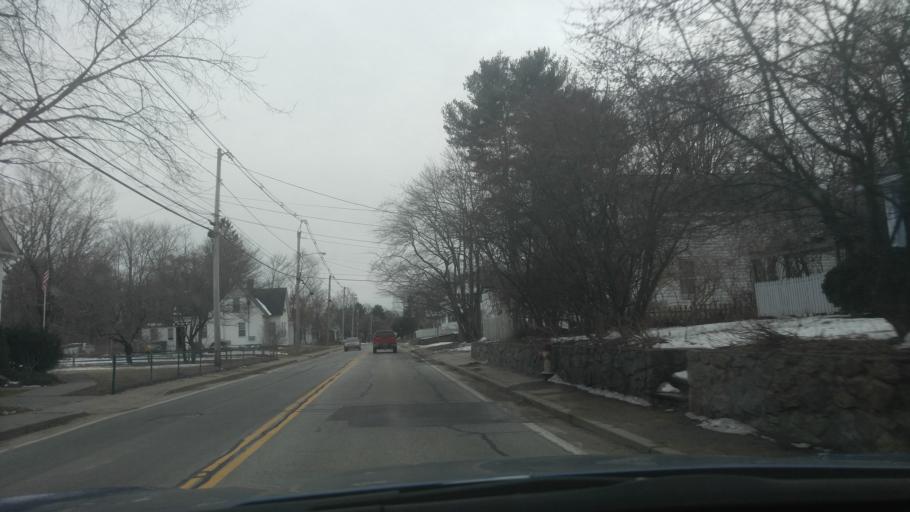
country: US
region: Rhode Island
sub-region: Kent County
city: West Warwick
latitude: 41.6852
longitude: -71.5673
